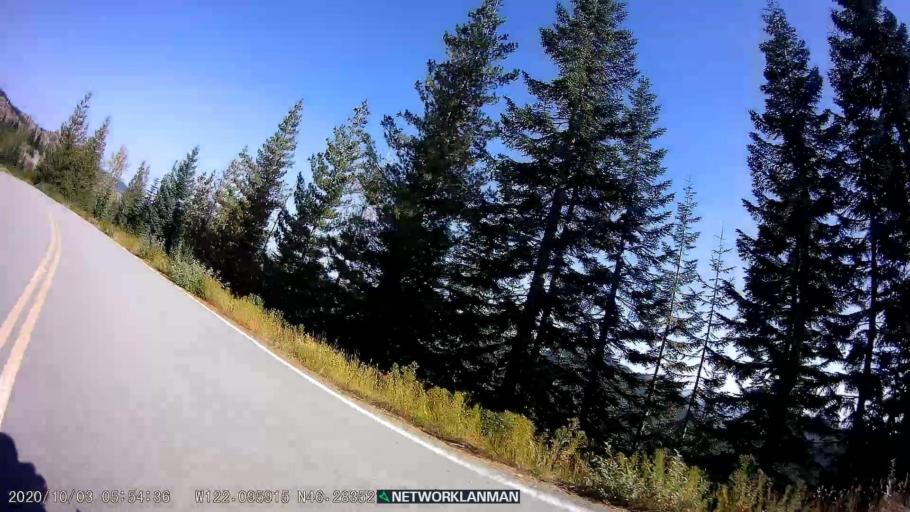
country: US
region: Washington
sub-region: Lewis County
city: Morton
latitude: 46.2815
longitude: -122.0972
